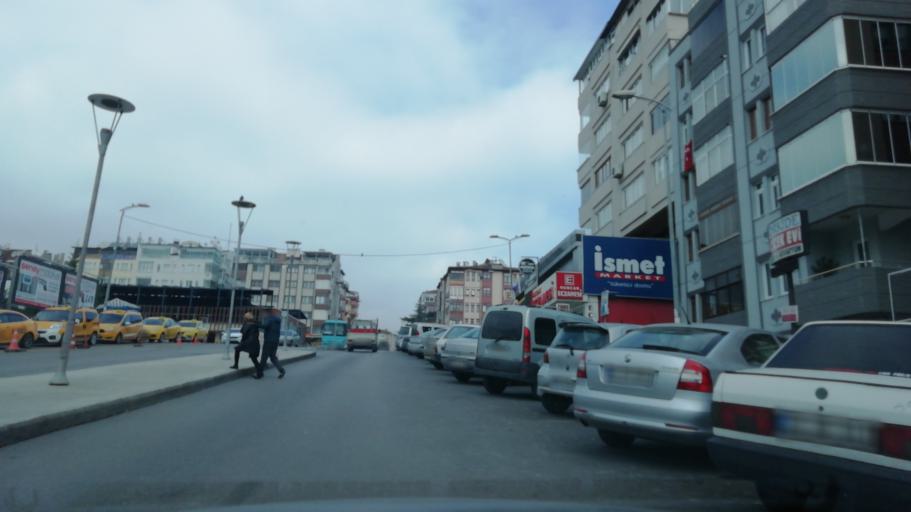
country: TR
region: Karabuk
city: Karabuk
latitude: 41.2085
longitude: 32.6200
